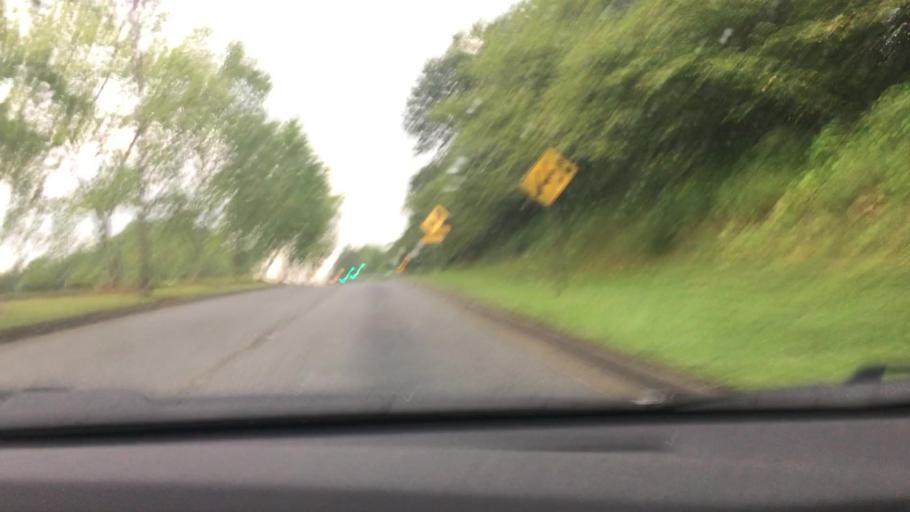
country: US
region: Georgia
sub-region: Fulton County
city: Union City
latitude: 33.6511
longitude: -84.5209
